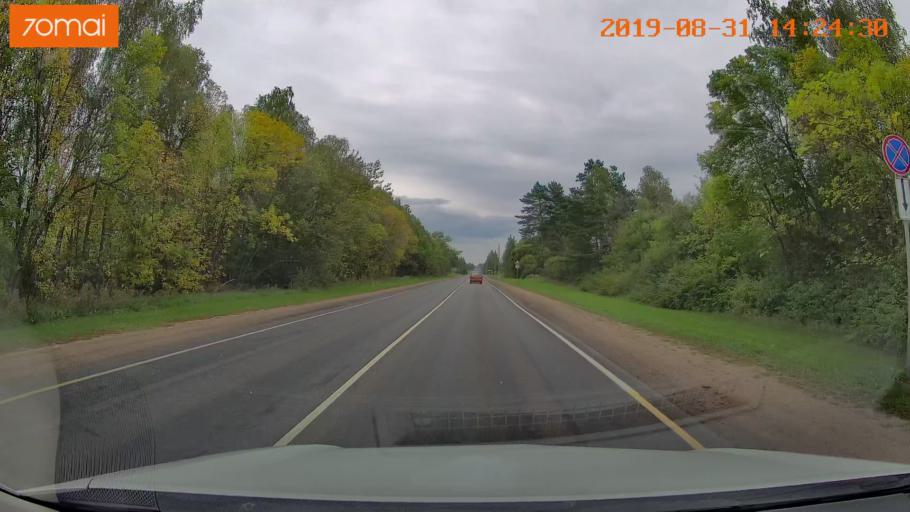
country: RU
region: Smolensk
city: Yekimovichi
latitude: 54.1033
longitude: 33.2565
